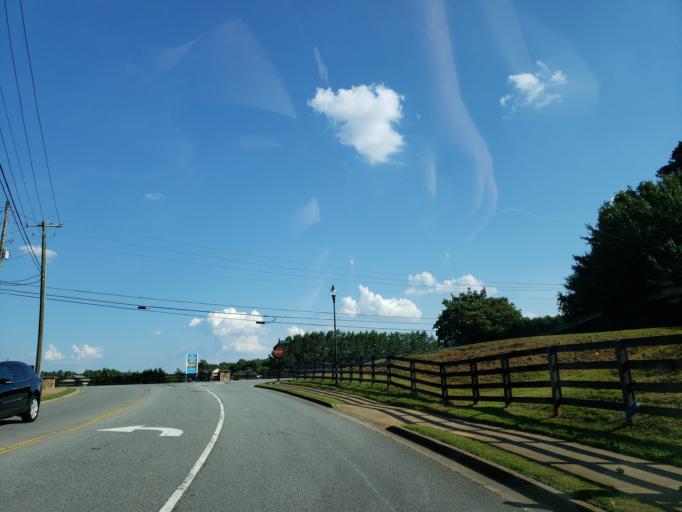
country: US
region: Georgia
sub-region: Cherokee County
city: Woodstock
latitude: 34.0960
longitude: -84.5355
